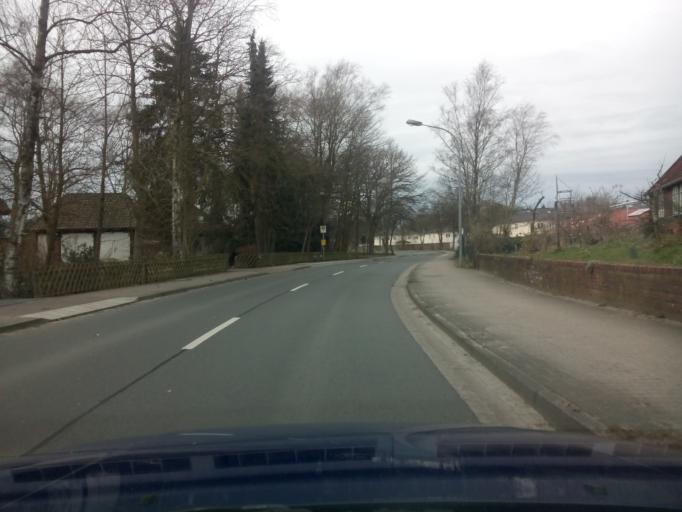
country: DE
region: Lower Saxony
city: Lilienthal
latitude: 53.1523
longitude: 8.9126
